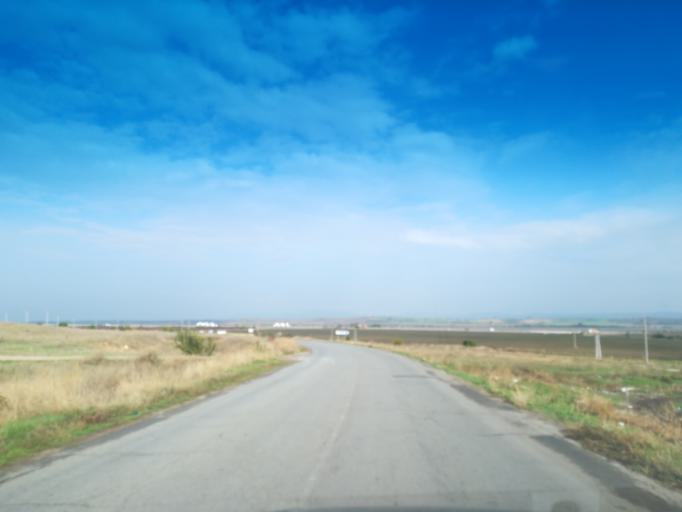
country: BG
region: Stara Zagora
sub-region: Obshtina Chirpan
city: Chirpan
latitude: 42.2039
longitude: 25.3088
